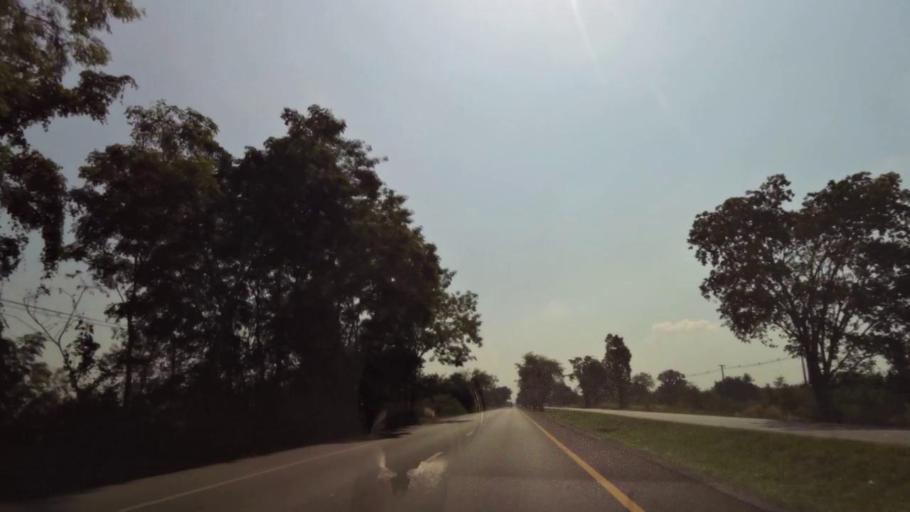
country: TH
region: Phichit
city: Bueng Na Rang
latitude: 16.2826
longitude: 100.1274
